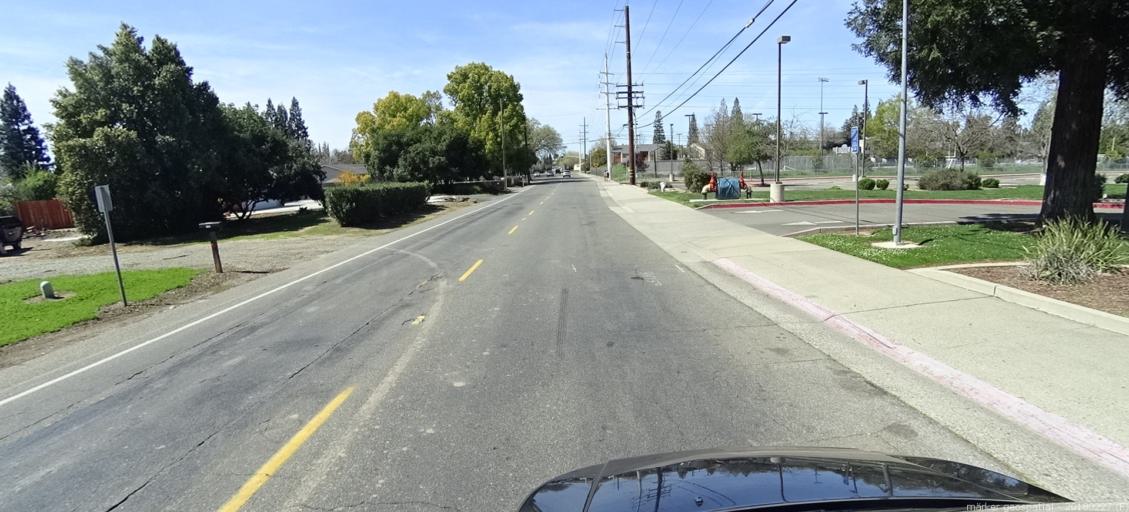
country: US
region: California
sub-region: Sacramento County
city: La Riviera
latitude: 38.5548
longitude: -121.3432
